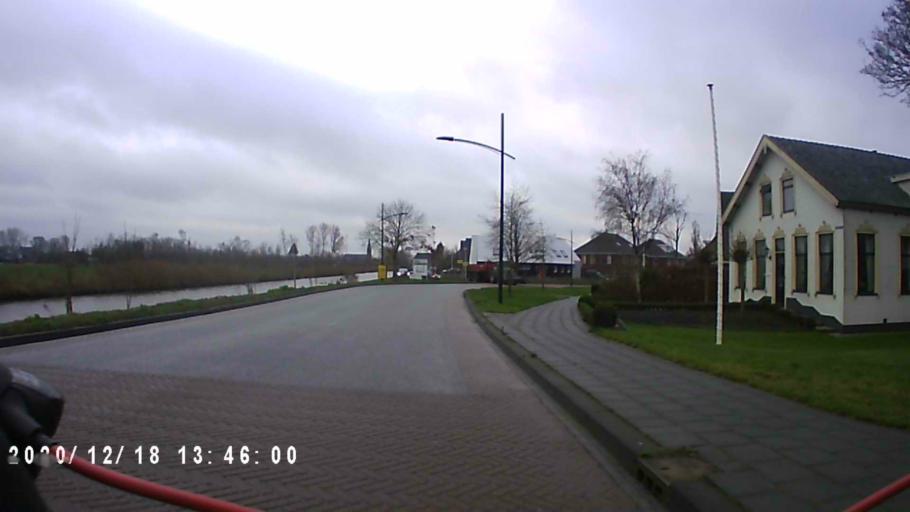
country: NL
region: Groningen
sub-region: Gemeente Bedum
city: Bedum
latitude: 53.3084
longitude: 6.6004
